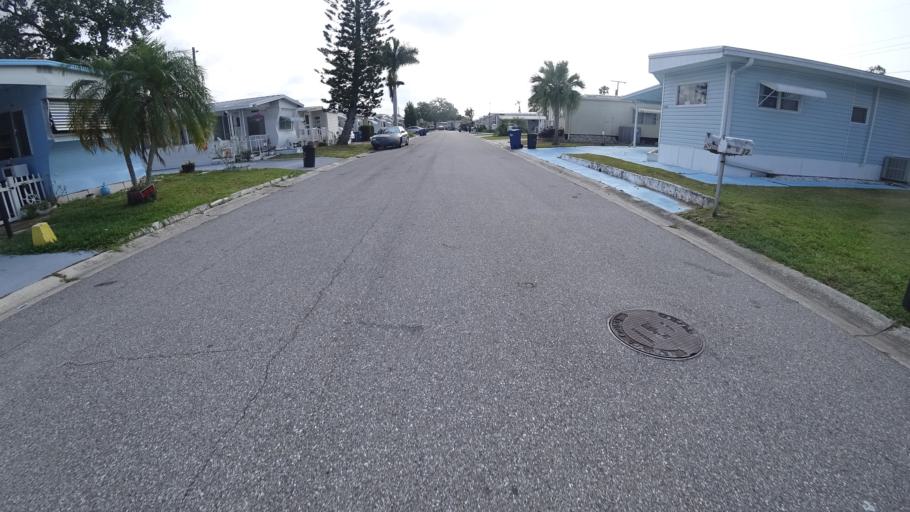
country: US
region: Florida
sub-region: Manatee County
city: South Bradenton
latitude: 27.4536
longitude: -82.5687
